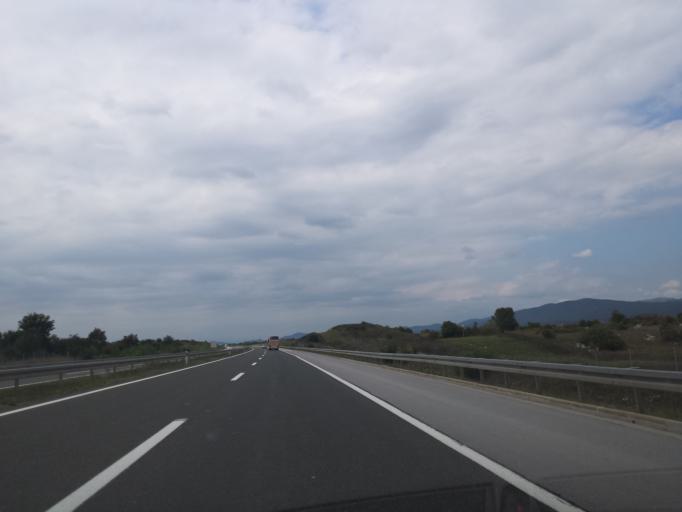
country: HR
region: Zadarska
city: Starigrad
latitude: 44.4662
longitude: 15.5973
